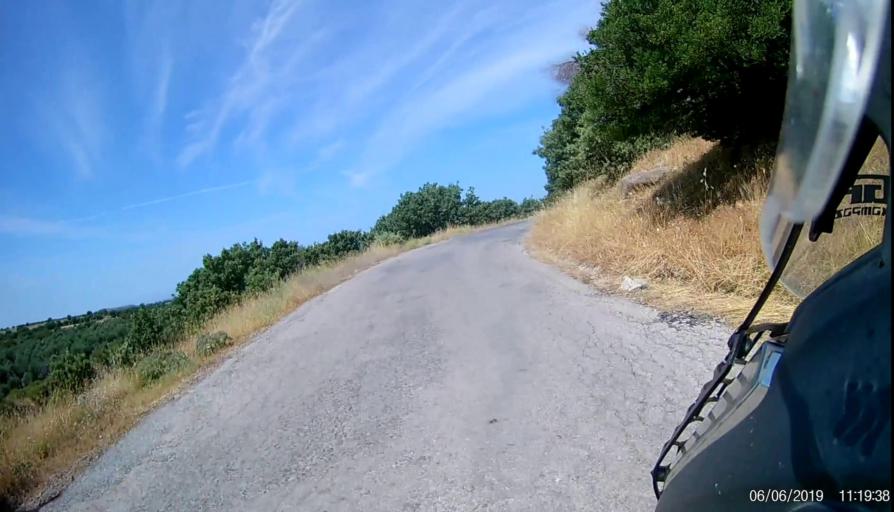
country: TR
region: Canakkale
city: Gulpinar
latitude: 39.6593
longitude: 26.1637
